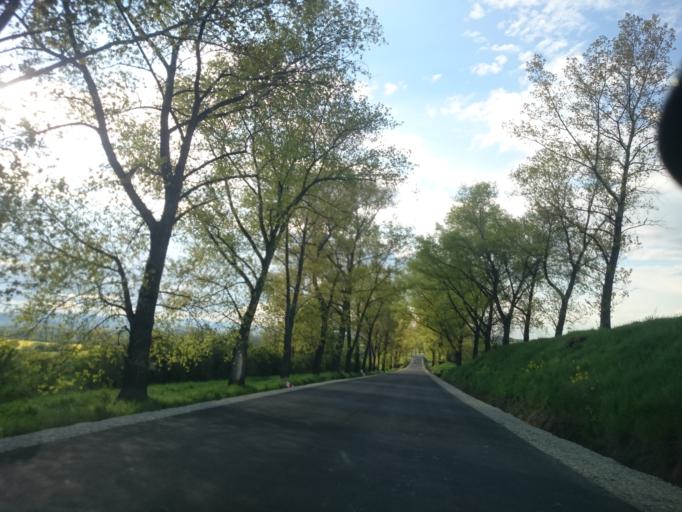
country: PL
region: Lower Silesian Voivodeship
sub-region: Powiat zabkowicki
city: Kamieniec Zabkowicki
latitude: 50.5587
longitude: 16.8514
